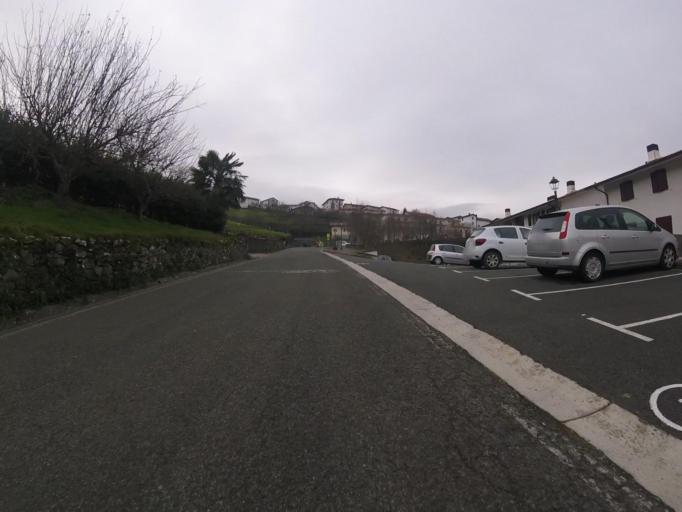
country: ES
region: Navarre
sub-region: Provincia de Navarra
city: Arantza
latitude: 43.1981
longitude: -1.7245
